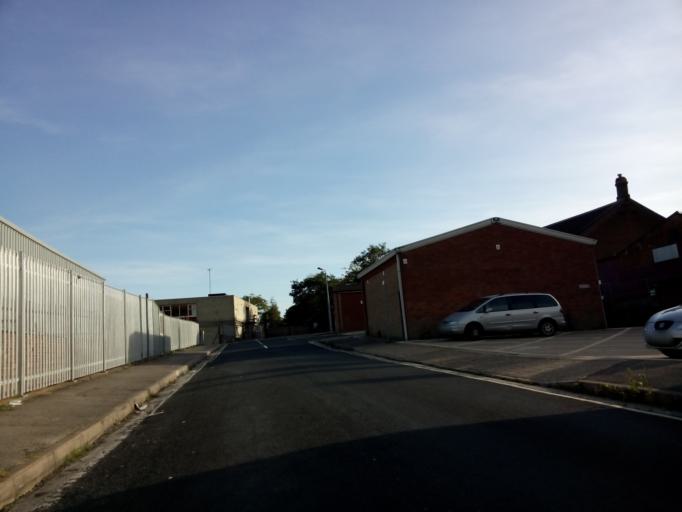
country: GB
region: England
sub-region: Suffolk
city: Ipswich
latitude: 52.0506
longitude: 1.1554
